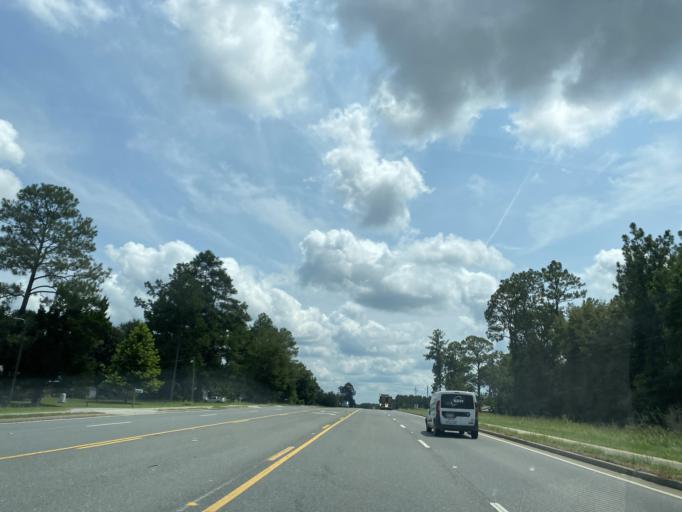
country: US
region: Georgia
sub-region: Ware County
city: Deenwood
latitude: 31.3431
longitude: -82.4638
